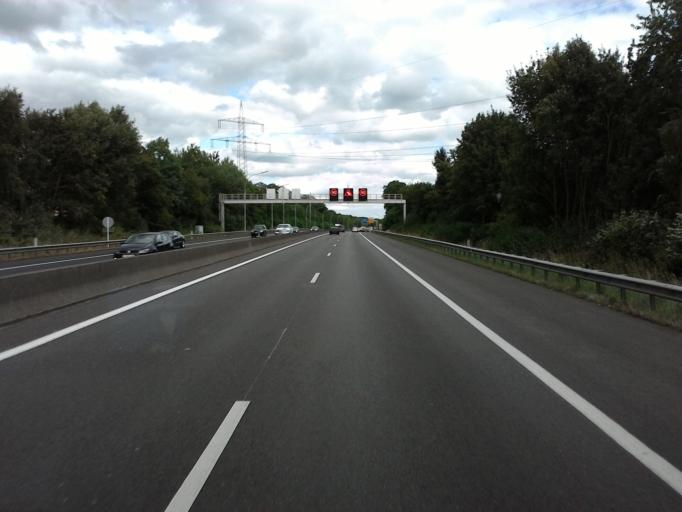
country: LU
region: Luxembourg
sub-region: Canton de Luxembourg
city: Strassen
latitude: 49.6303
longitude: 6.0564
